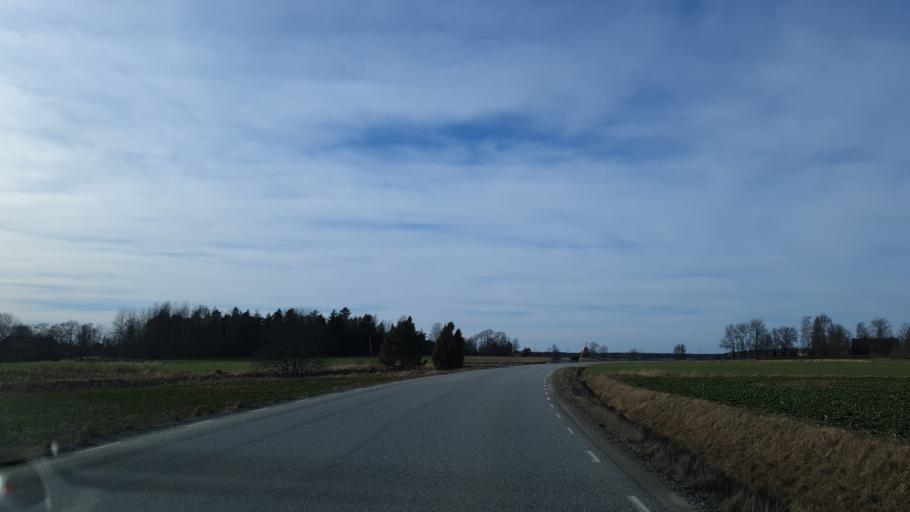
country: SE
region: Uppsala
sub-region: Enkopings Kommun
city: Grillby
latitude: 59.5788
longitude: 17.2205
